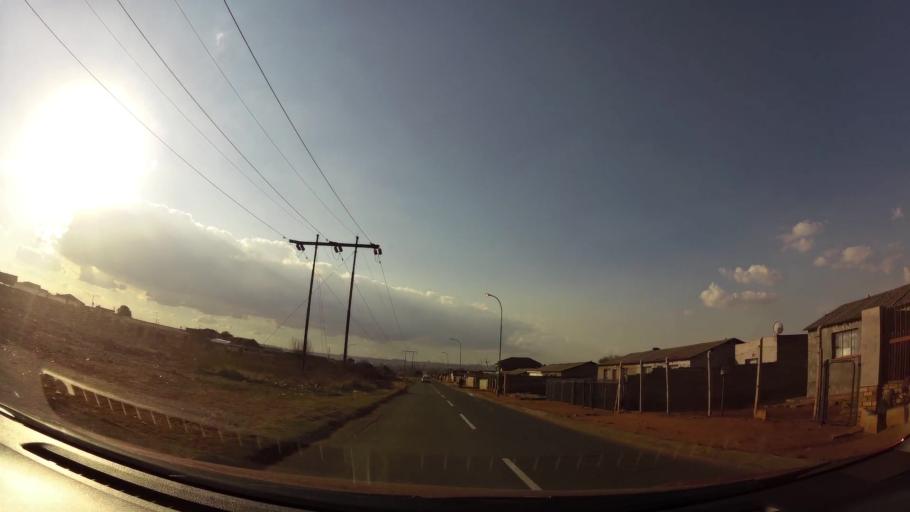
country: ZA
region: Gauteng
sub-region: City of Johannesburg Metropolitan Municipality
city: Soweto
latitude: -26.2301
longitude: 27.8586
